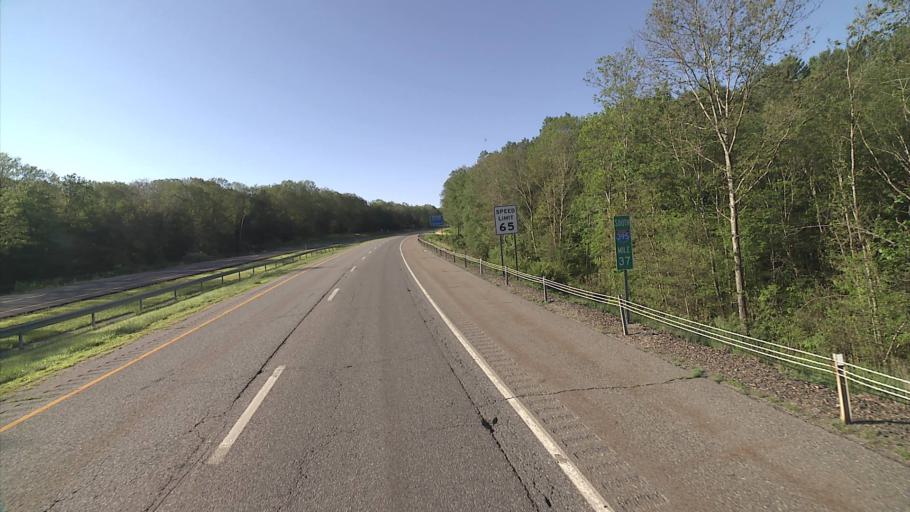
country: US
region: Connecticut
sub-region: Windham County
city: Danielson
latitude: 41.7855
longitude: -71.8725
